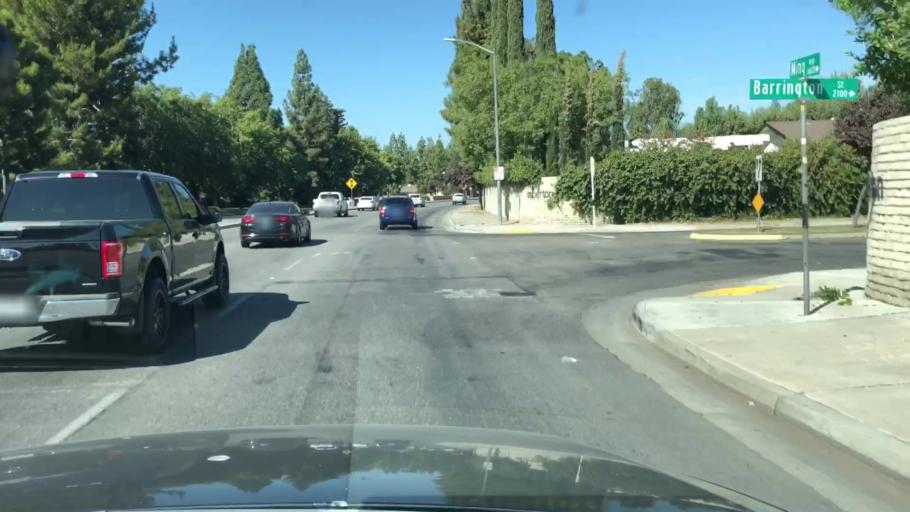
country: US
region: California
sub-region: Kern County
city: Greenacres
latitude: 35.3349
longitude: -119.0768
